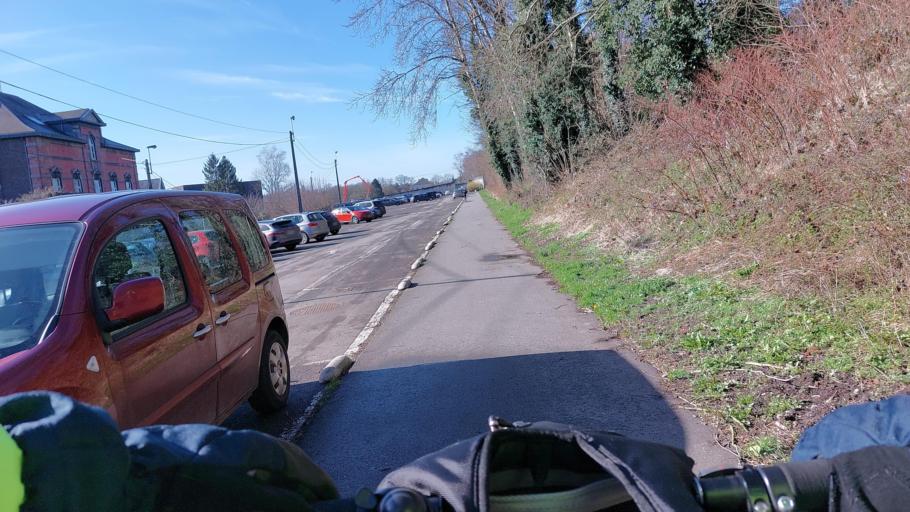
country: BE
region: Wallonia
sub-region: Province du Brabant Wallon
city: Nivelles
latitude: 50.6011
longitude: 4.3229
